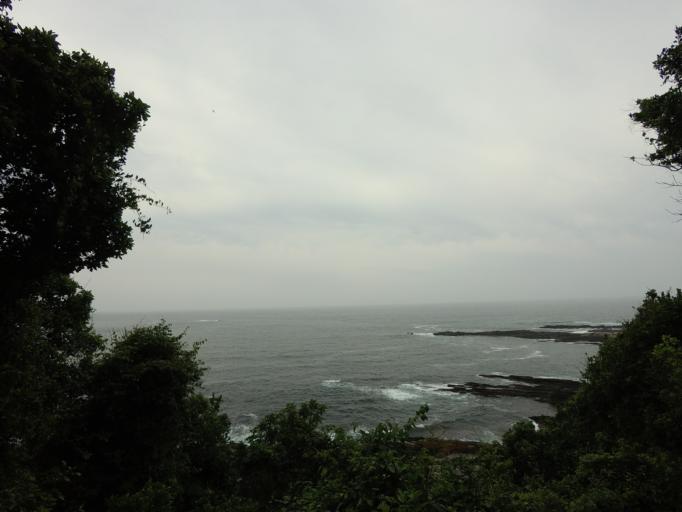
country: ZA
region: Eastern Cape
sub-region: Cacadu District Municipality
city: Kareedouw
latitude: -34.0205
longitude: 23.9004
